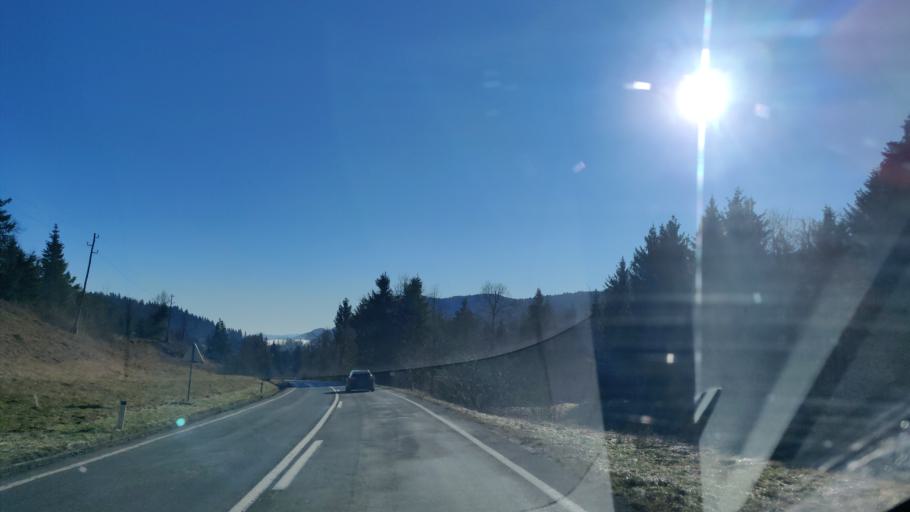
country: SI
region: Logatec
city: Logatec
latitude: 45.8821
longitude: 14.2042
